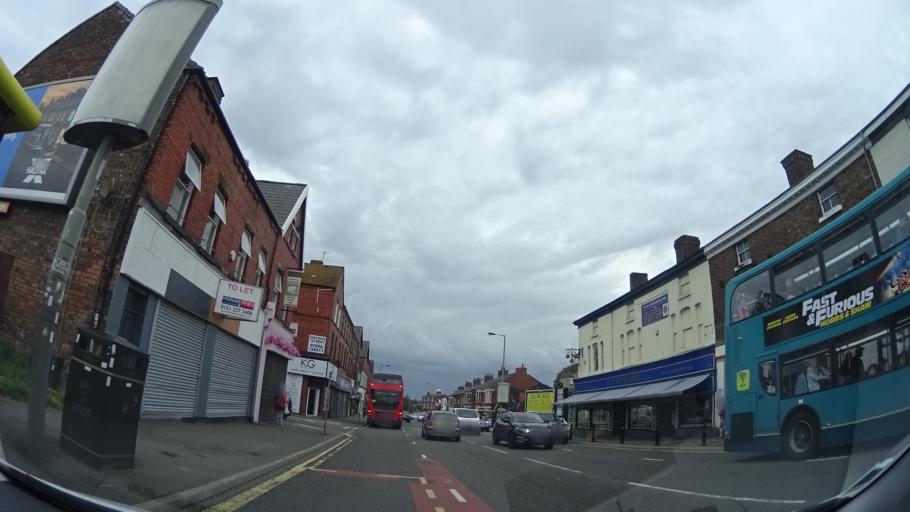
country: GB
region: England
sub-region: Liverpool
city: Liverpool
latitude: 53.4141
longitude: -2.9154
